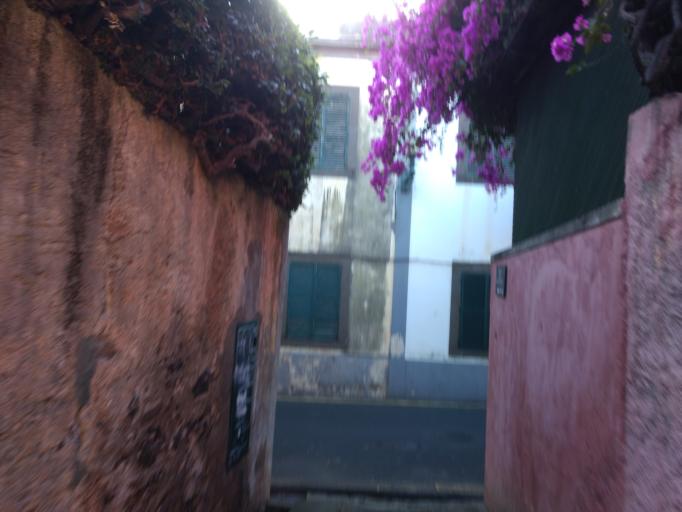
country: PT
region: Madeira
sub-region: Funchal
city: Funchal
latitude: 32.6464
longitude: -16.9203
